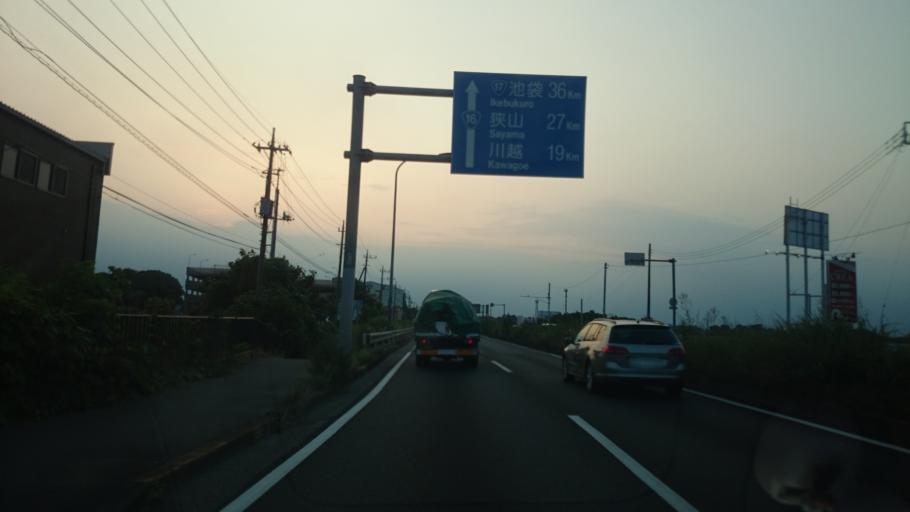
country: JP
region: Saitama
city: Hasuda
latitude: 35.9594
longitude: 139.6532
